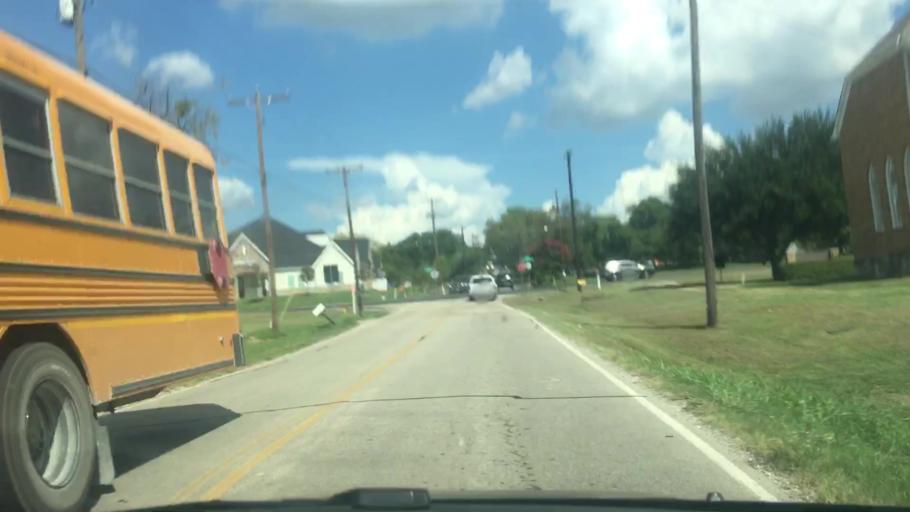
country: US
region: Texas
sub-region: Collin County
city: Prosper
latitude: 33.2336
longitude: -96.8023
